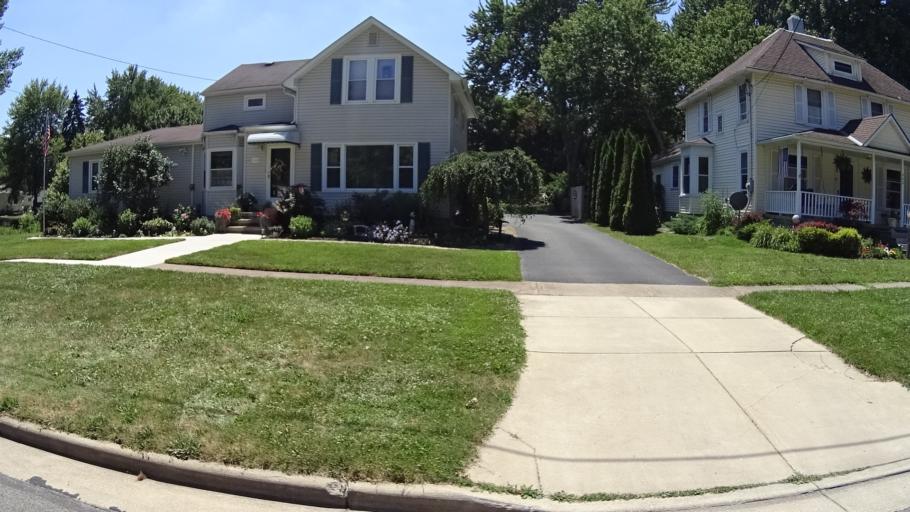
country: US
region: Ohio
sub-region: Erie County
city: Huron
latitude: 41.3922
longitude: -82.5619
